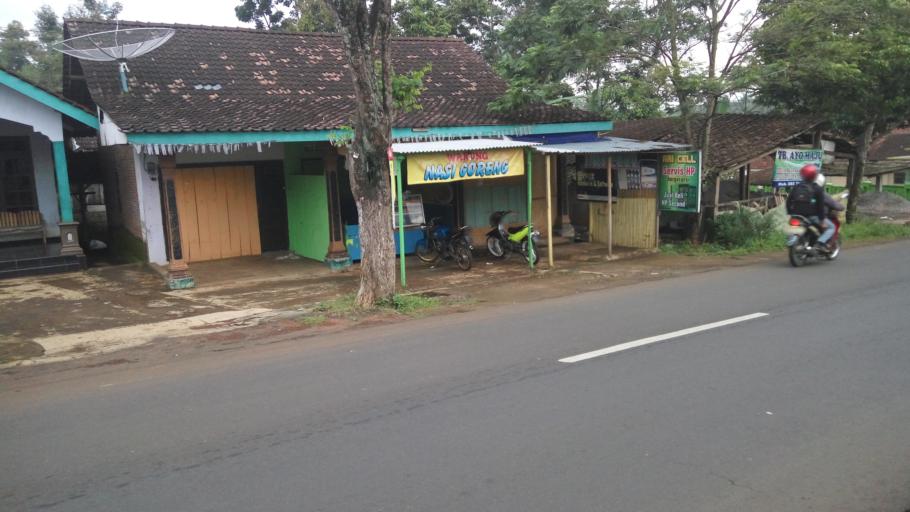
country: ID
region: Central Java
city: Ambarawa
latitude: -7.2409
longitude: 110.4236
